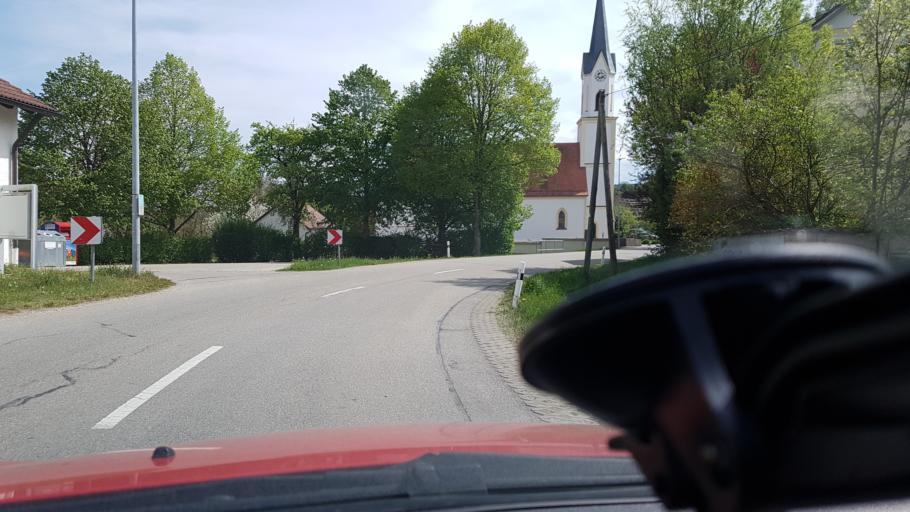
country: DE
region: Bavaria
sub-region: Lower Bavaria
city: Stubenberg
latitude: 48.3409
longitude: 13.0852
